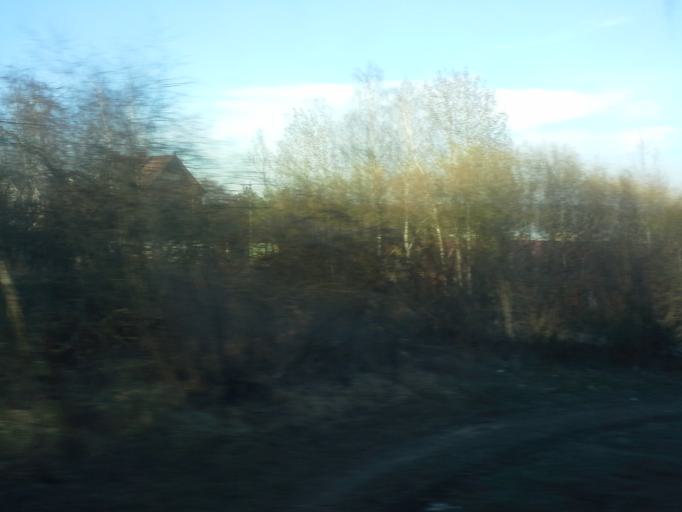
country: RU
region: Moskovskaya
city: Yermolino
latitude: 56.1334
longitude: 37.5192
